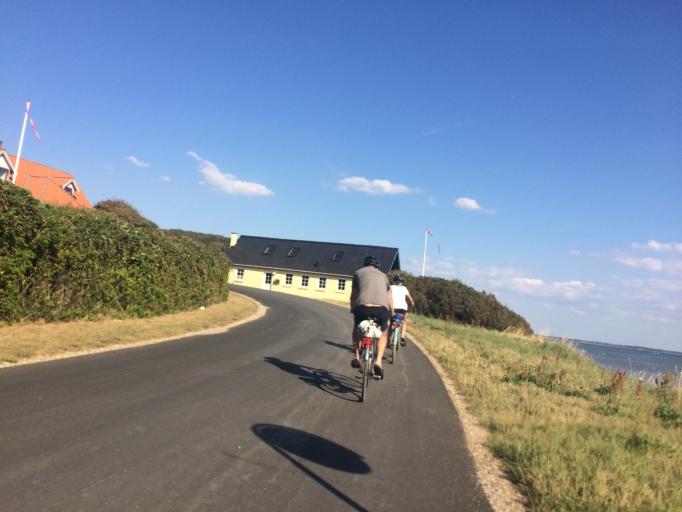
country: DK
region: Central Jutland
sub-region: Holstebro Kommune
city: Vinderup
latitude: 56.5803
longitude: 8.7126
